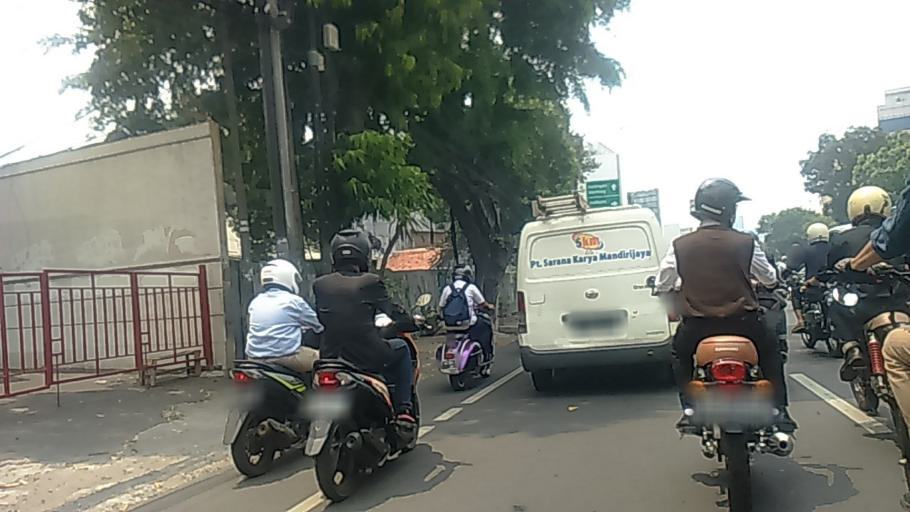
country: ID
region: Jakarta Raya
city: Jakarta
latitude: -6.2560
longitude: 106.8278
